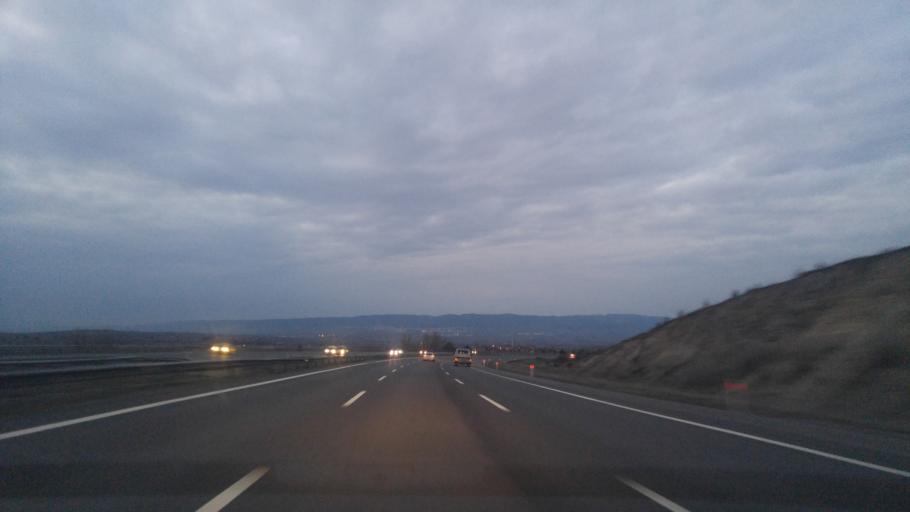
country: TR
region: Bolu
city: Gerede
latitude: 40.6557
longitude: 32.2370
